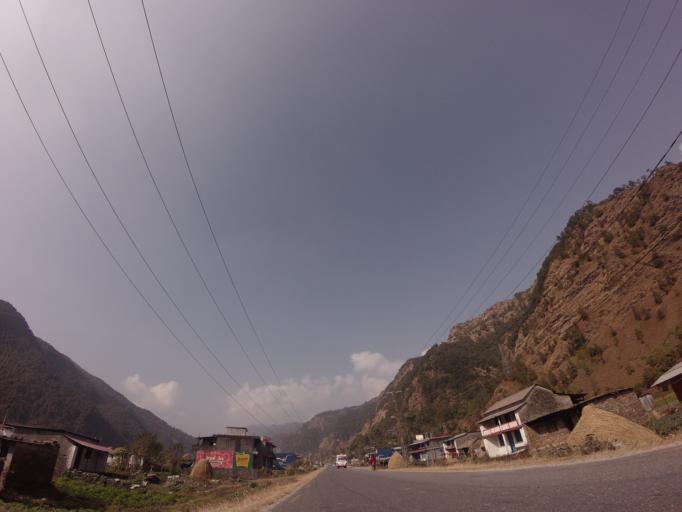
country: NP
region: Western Region
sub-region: Gandaki Zone
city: Pokhara
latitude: 28.2863
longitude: 83.9008
